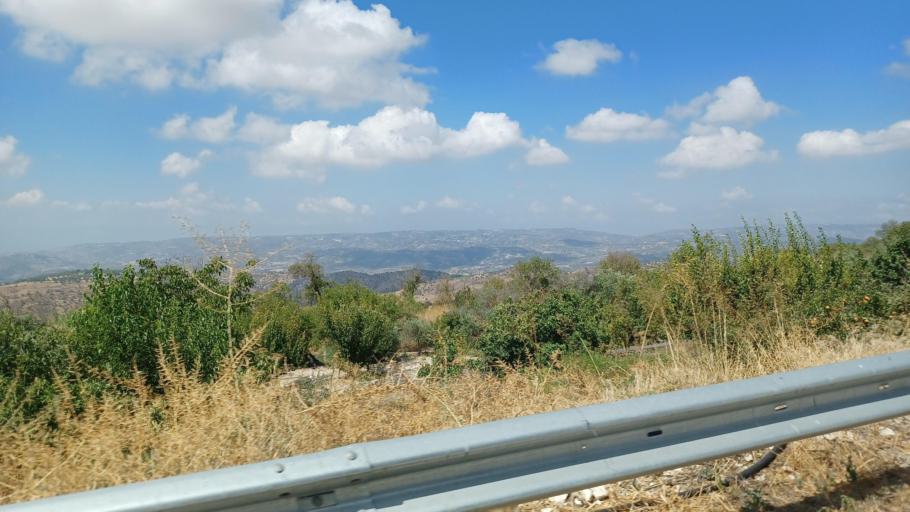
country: CY
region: Pafos
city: Mesogi
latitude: 34.8767
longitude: 32.6099
